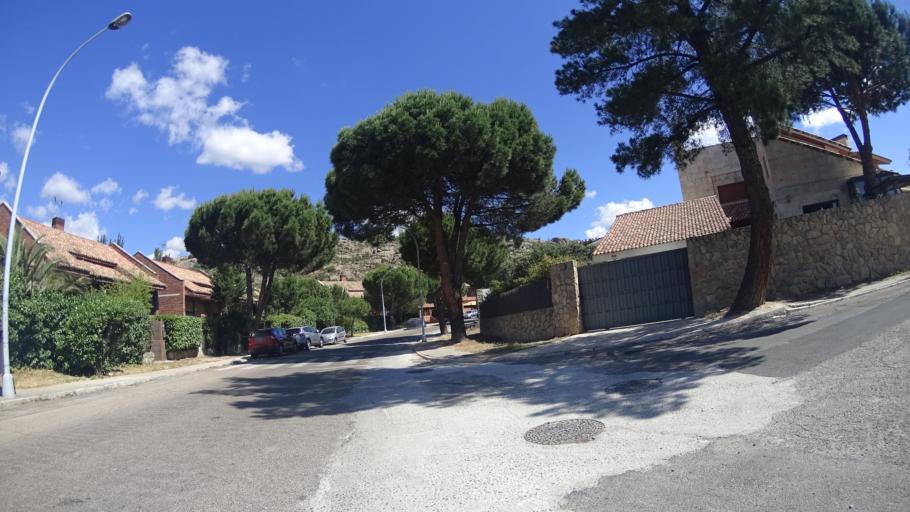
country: ES
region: Madrid
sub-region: Provincia de Madrid
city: Torrelodones
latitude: 40.5841
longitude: -3.9248
